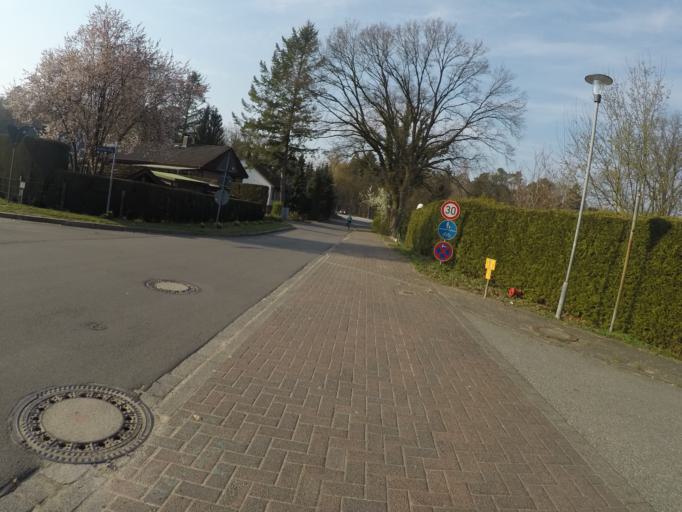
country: DE
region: Schleswig-Holstein
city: Wittenborn
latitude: 53.9239
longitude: 10.2212
